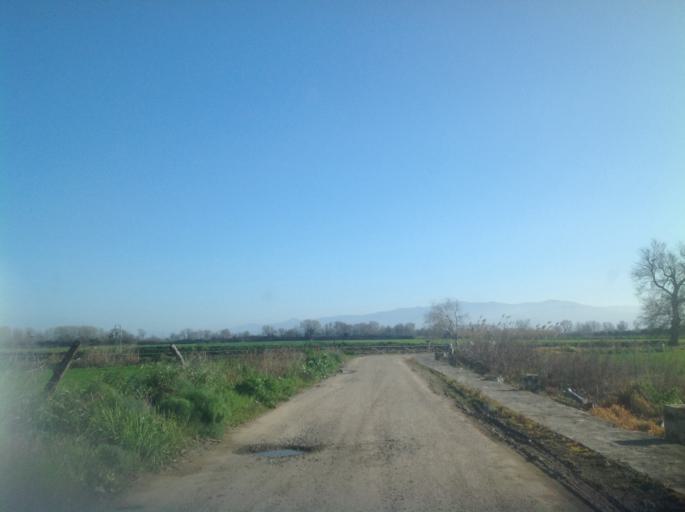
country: IT
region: Calabria
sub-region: Provincia di Cosenza
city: Sibari
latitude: 39.7191
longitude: 16.4969
